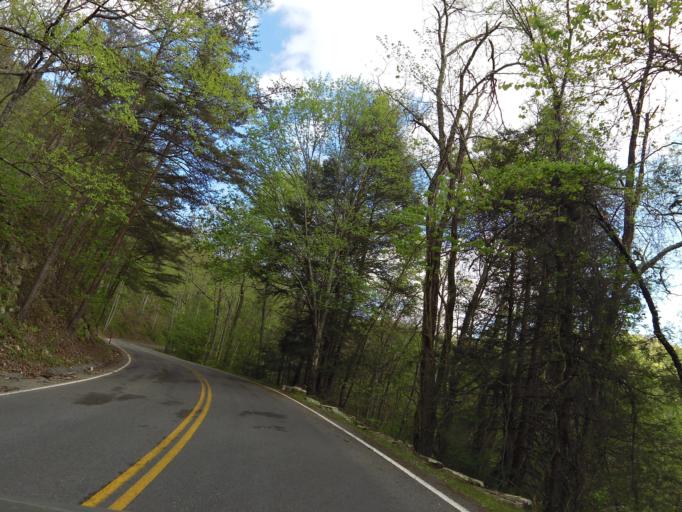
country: US
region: Tennessee
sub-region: Claiborne County
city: Harrogate
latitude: 36.6075
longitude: -83.6760
